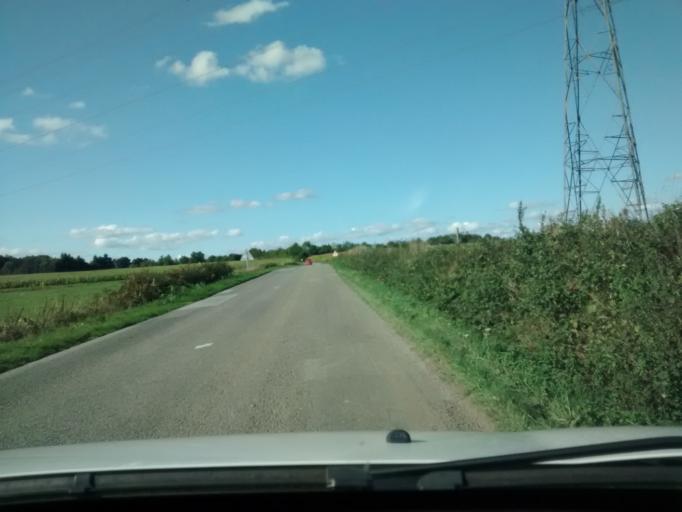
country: FR
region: Brittany
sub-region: Departement d'Ille-et-Vilaine
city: Noyal-sur-Vilaine
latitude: 48.0812
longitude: -1.5464
